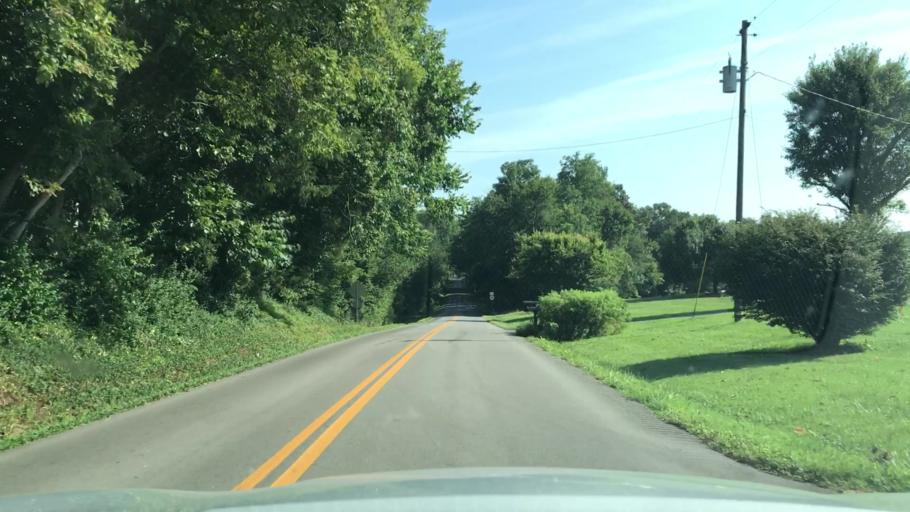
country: US
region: Kentucky
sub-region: Clinton County
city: Albany
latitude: 36.6669
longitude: -85.0720
